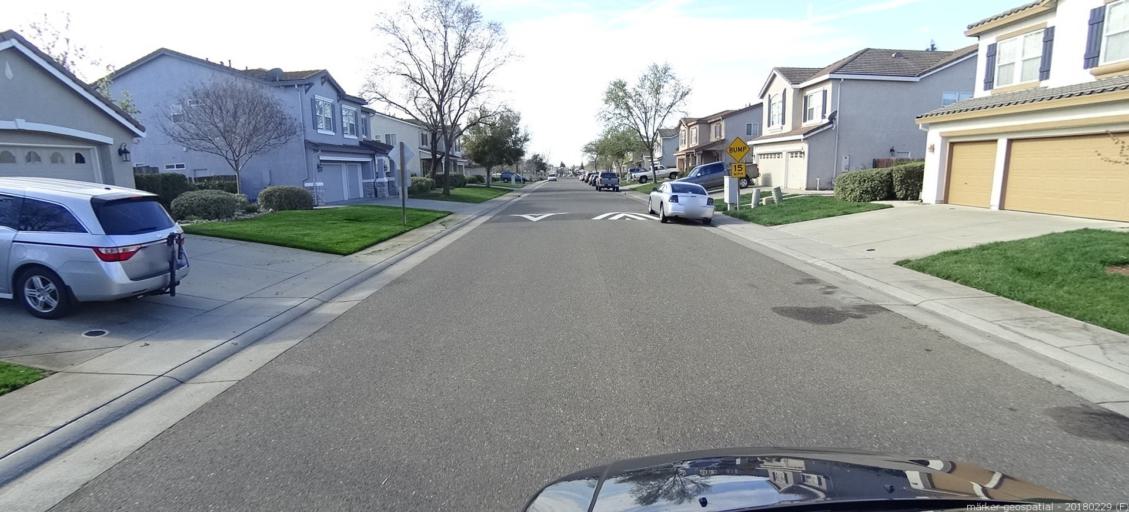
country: US
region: California
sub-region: Sacramento County
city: Rancho Cordova
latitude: 38.5480
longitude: -121.2768
